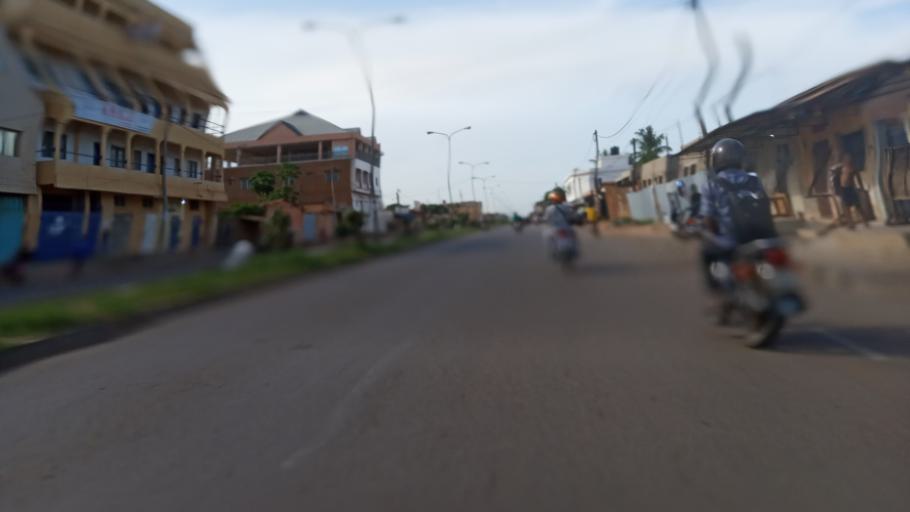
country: TG
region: Maritime
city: Lome
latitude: 6.1662
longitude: 1.2668
